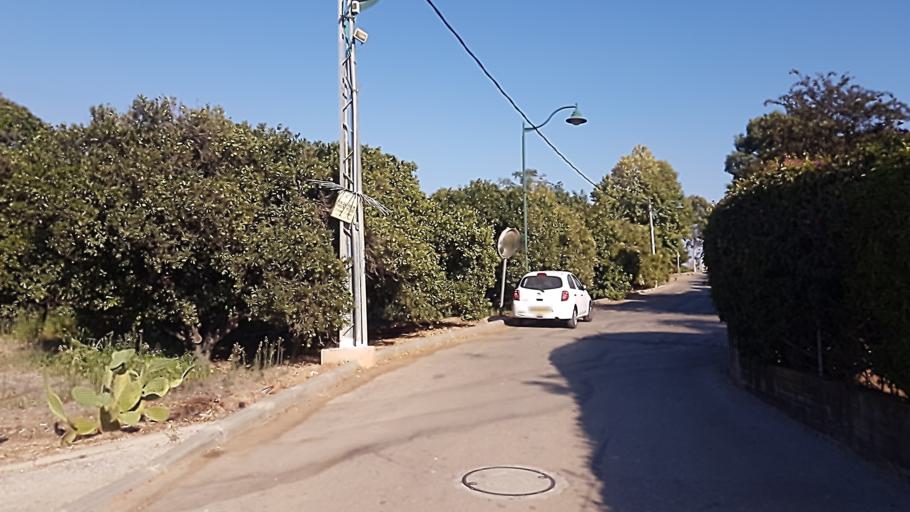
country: IL
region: Central District
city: Kfar Saba
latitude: 32.2035
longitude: 34.9131
